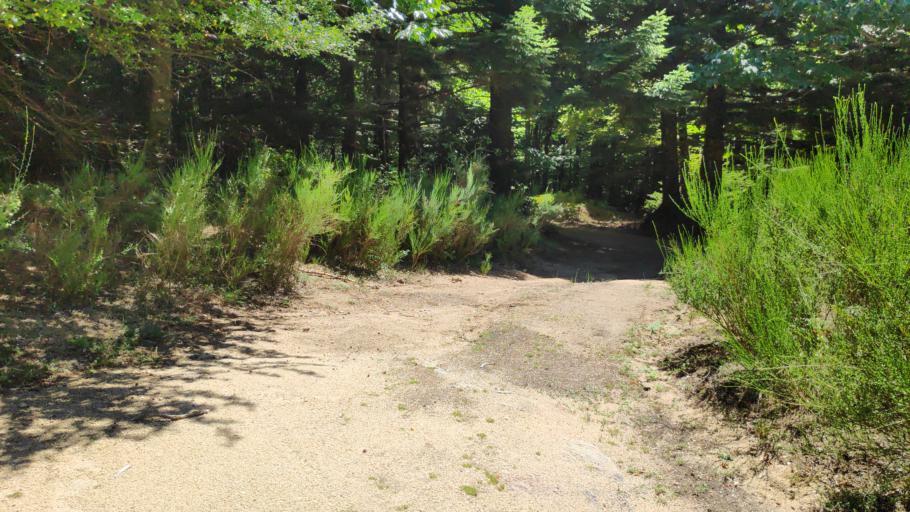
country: IT
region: Calabria
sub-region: Provincia di Vibo-Valentia
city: Mongiana
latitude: 38.5328
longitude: 16.3757
